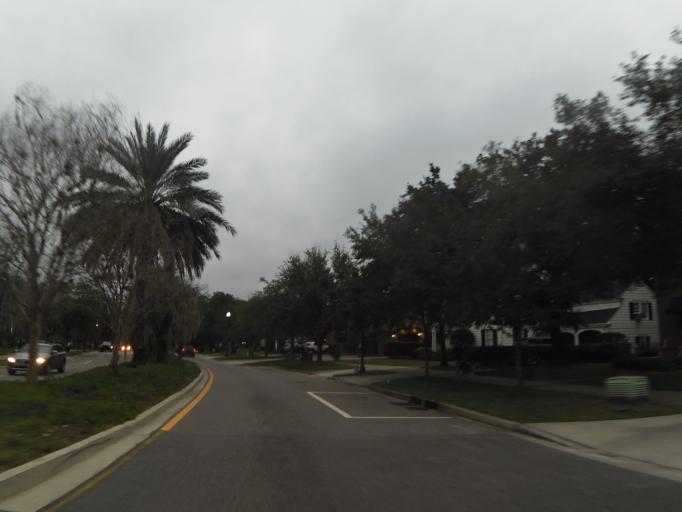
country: US
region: Florida
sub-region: Duval County
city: Jacksonville
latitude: 30.3048
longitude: -81.6585
